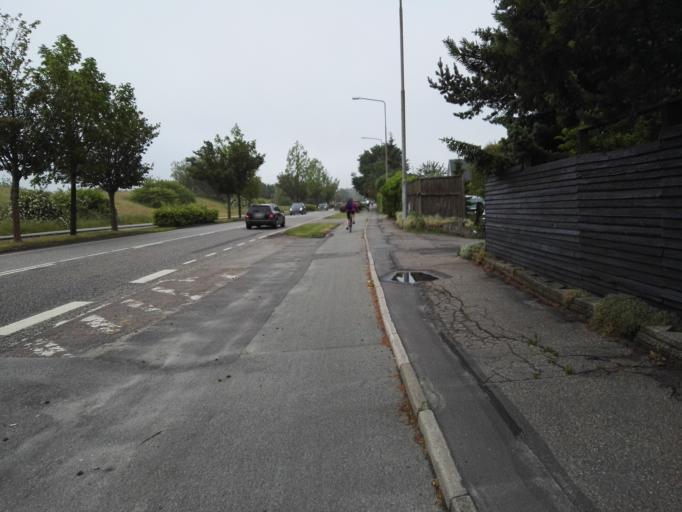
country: DK
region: Capital Region
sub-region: Ballerup Kommune
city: Ballerup
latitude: 55.7503
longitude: 12.3726
